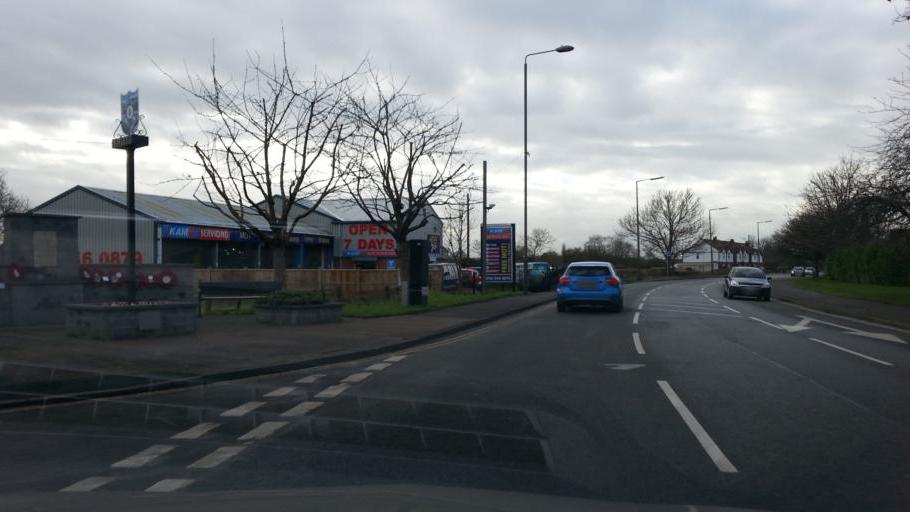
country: GB
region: England
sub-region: Derbyshire
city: Long Eaton
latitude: 52.8799
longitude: -1.2936
